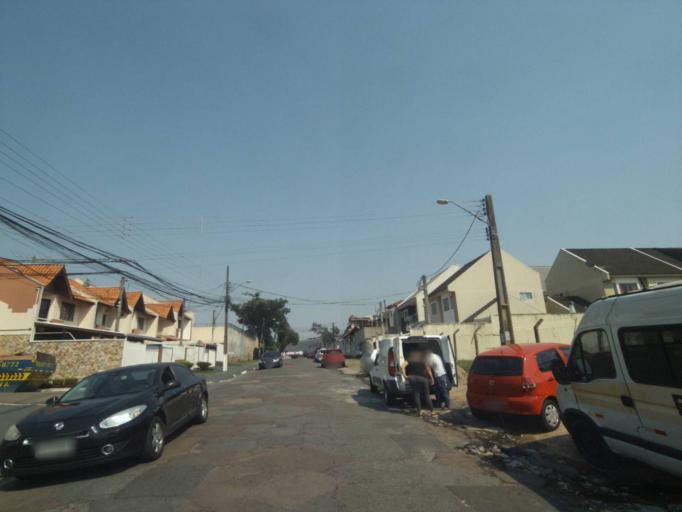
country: BR
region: Parana
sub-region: Sao Jose Dos Pinhais
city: Sao Jose dos Pinhais
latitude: -25.5193
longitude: -49.2538
